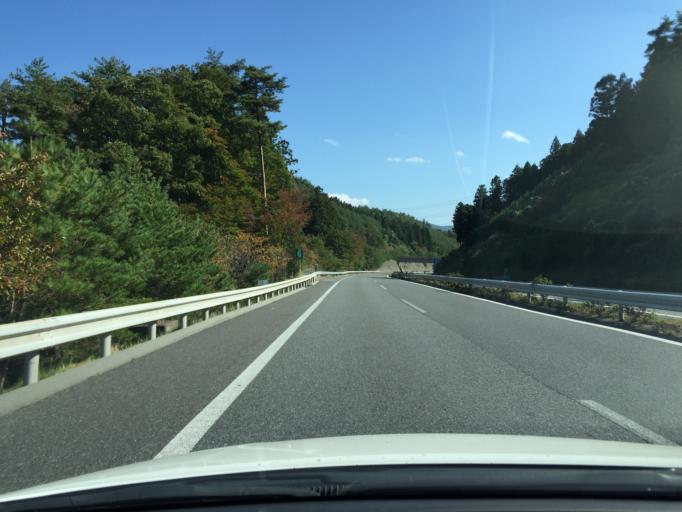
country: JP
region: Fukushima
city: Iwaki
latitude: 37.1521
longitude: 140.7376
